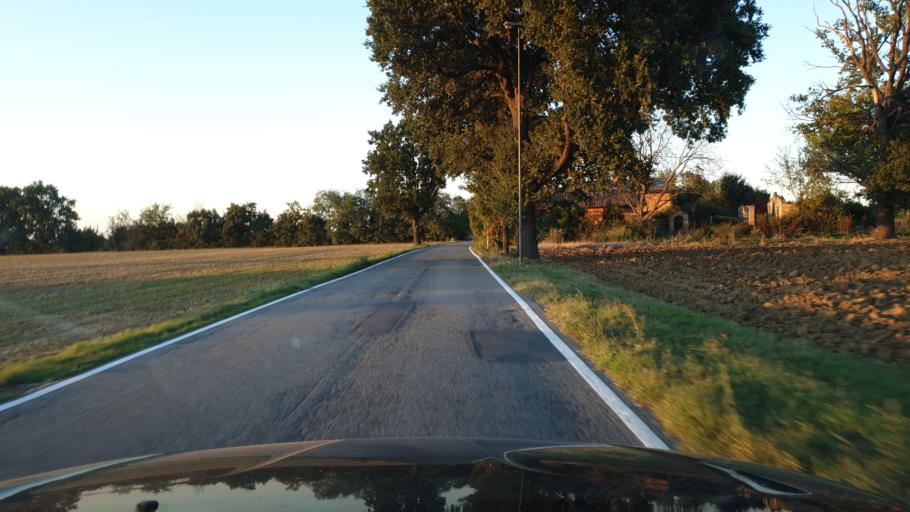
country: IT
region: Emilia-Romagna
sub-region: Provincia di Bologna
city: Quarto Inferiore
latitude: 44.5246
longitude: 11.3923
